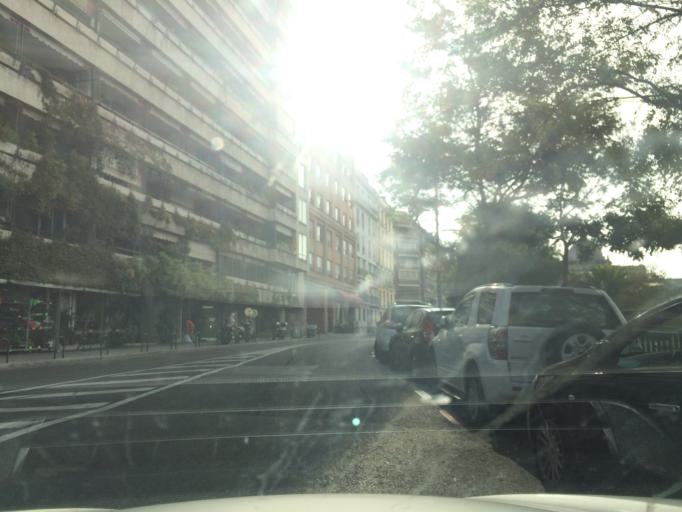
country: ES
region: Madrid
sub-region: Provincia de Madrid
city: City Center
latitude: 40.4226
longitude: -3.7196
